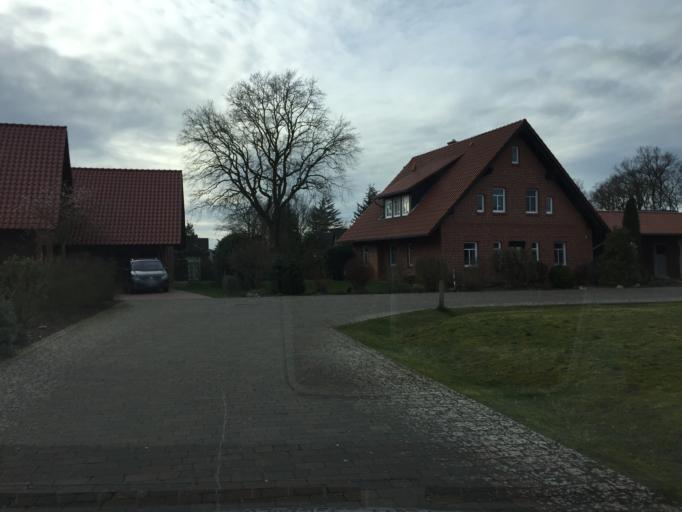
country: DE
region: Lower Saxony
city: Scholen
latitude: 52.6967
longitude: 8.7683
